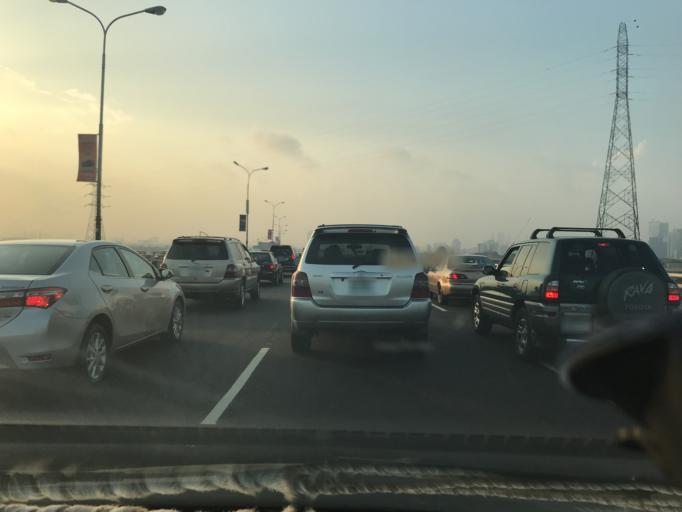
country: NG
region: Lagos
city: Lagos
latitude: 6.4683
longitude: 3.3910
